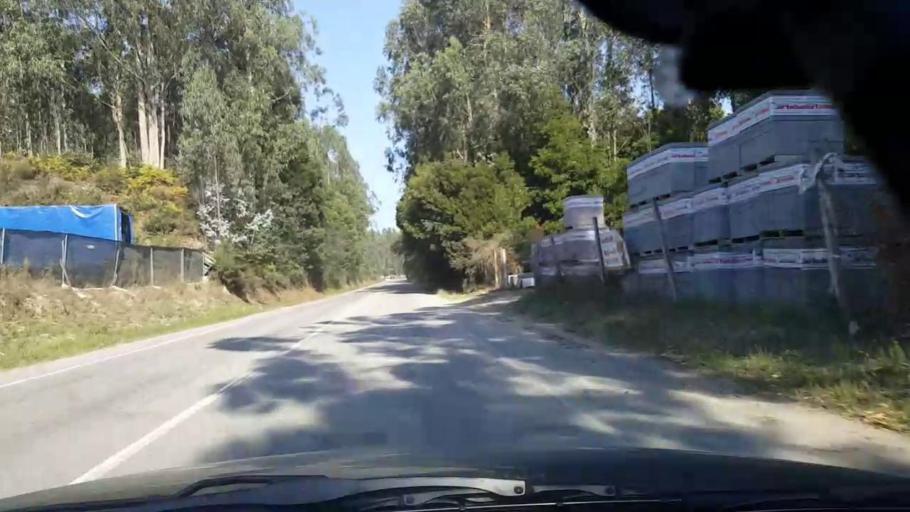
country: PT
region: Porto
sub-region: Vila do Conde
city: Arvore
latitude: 41.3514
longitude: -8.6852
